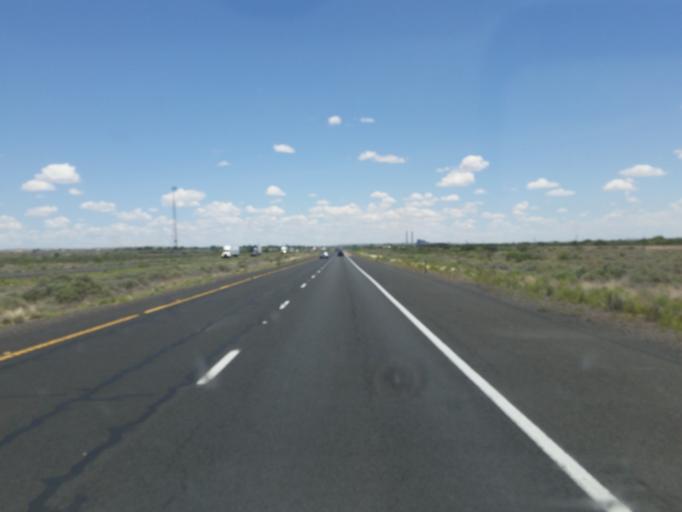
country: US
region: Arizona
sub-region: Navajo County
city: Joseph City
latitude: 34.9612
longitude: -110.3841
